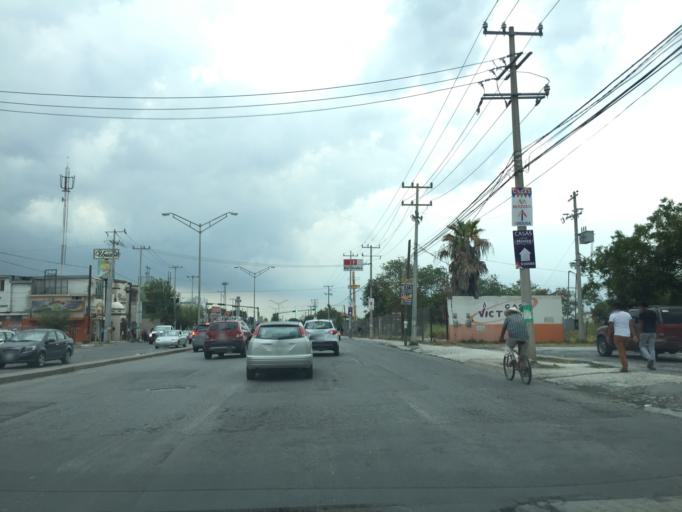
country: MX
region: Nuevo Leon
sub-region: Juarez
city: Valle de Juarez
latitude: 25.6599
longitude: -100.1794
